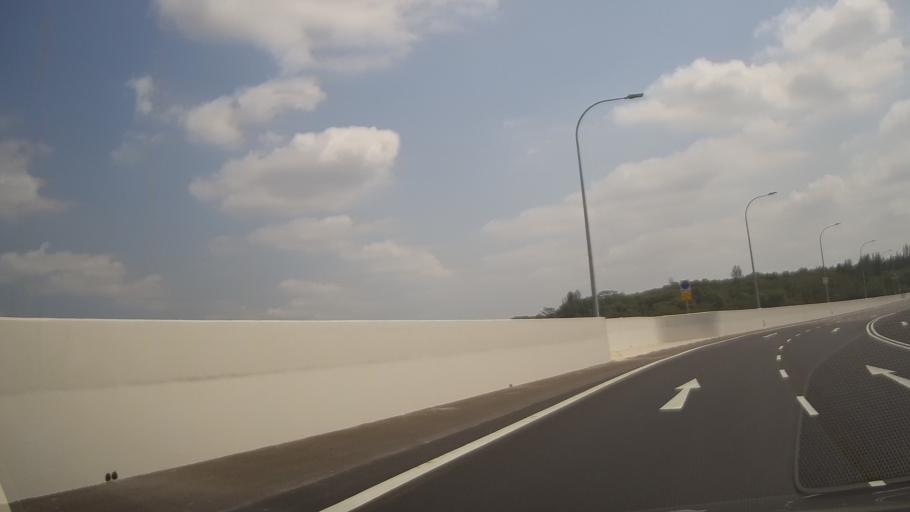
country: MY
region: Johor
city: Kampung Pasir Gudang Baru
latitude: 1.3827
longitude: 103.9150
